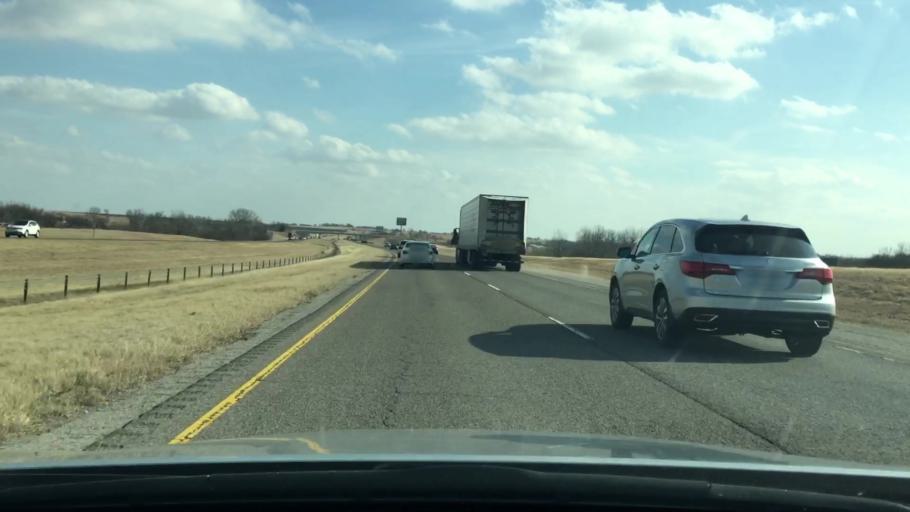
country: US
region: Oklahoma
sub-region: Garvin County
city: Maysville
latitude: 34.9030
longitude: -97.3507
